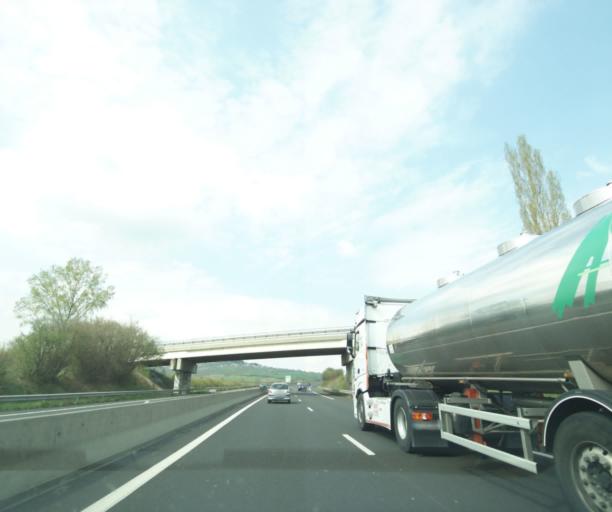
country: FR
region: Auvergne
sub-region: Departement du Puy-de-Dome
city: Tallende
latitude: 45.6677
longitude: 3.1438
